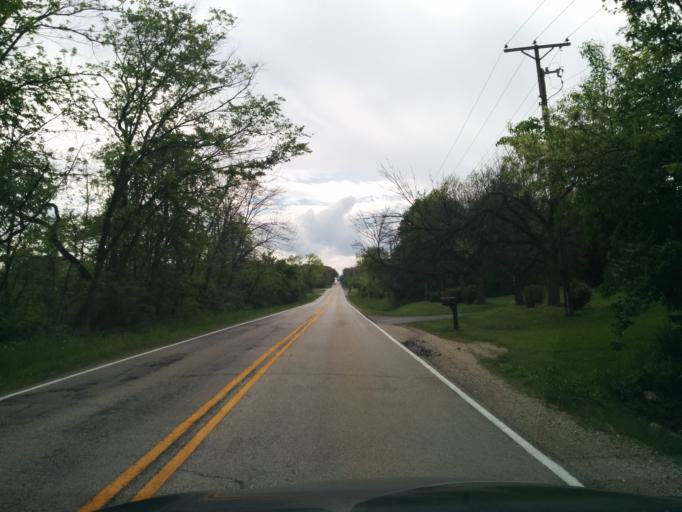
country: US
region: Illinois
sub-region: Cook County
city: Lemont
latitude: 41.6417
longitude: -88.0160
